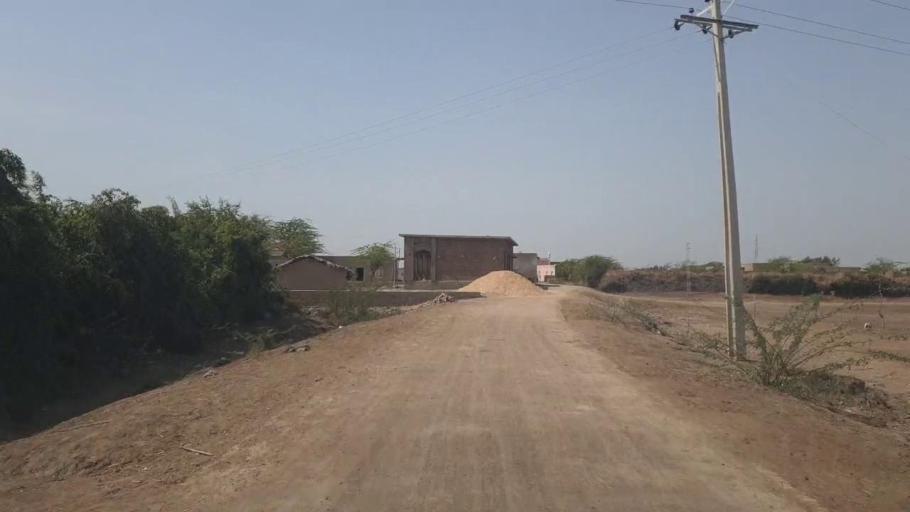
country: PK
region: Sindh
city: Dhoro Naro
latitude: 25.4093
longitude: 69.5791
